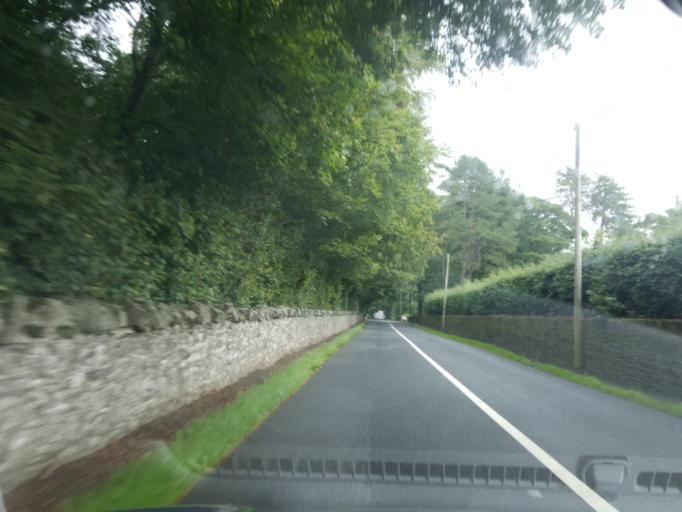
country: IE
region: Leinster
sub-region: Kildare
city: Kilcullen
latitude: 53.1209
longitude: -6.7083
